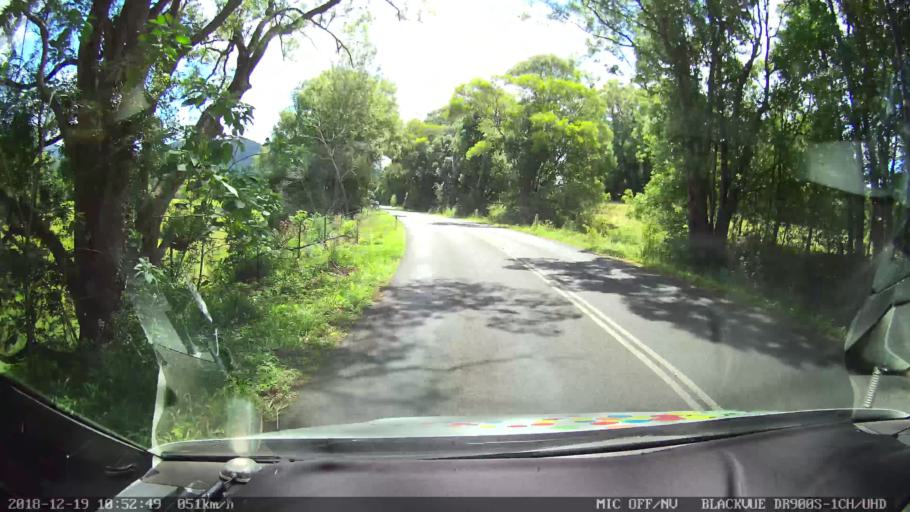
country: AU
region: New South Wales
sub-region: Lismore Municipality
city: Nimbin
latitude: -28.5913
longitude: 153.2332
